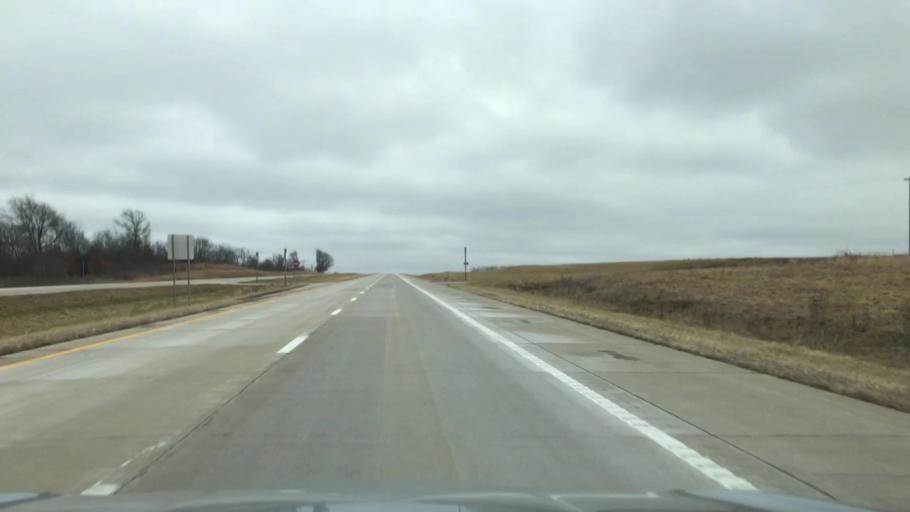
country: US
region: Missouri
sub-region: Livingston County
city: Chillicothe
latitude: 39.7381
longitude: -93.6956
